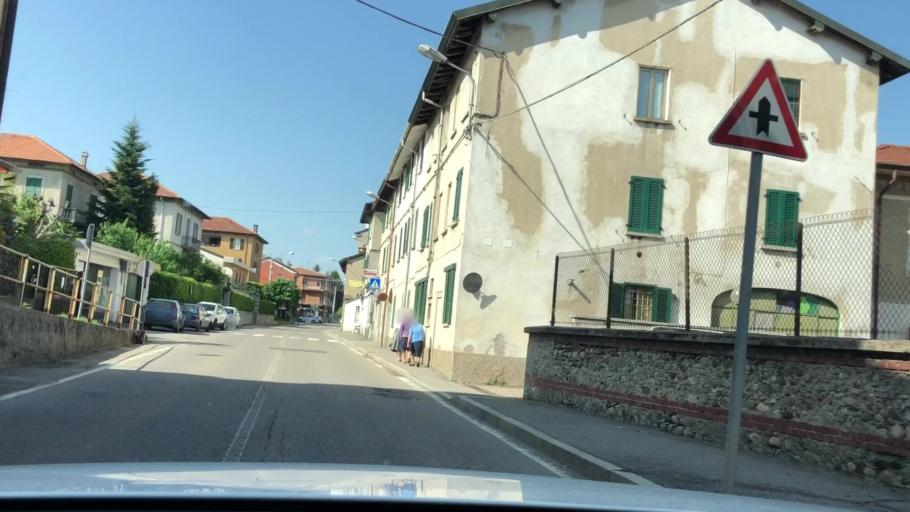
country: IT
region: Lombardy
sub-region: Provincia di Como
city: Lomazzo
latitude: 45.7102
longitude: 9.0393
